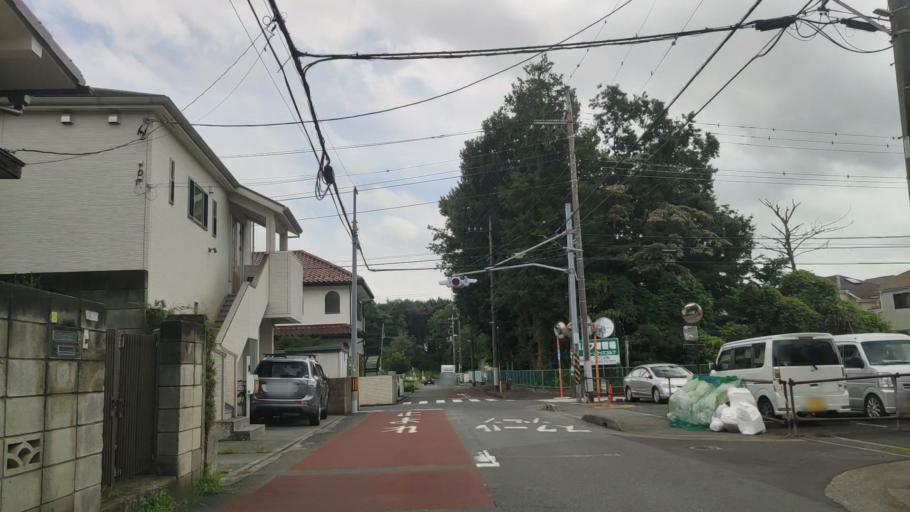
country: JP
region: Tokyo
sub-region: Machida-shi
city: Machida
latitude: 35.5166
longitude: 139.4452
